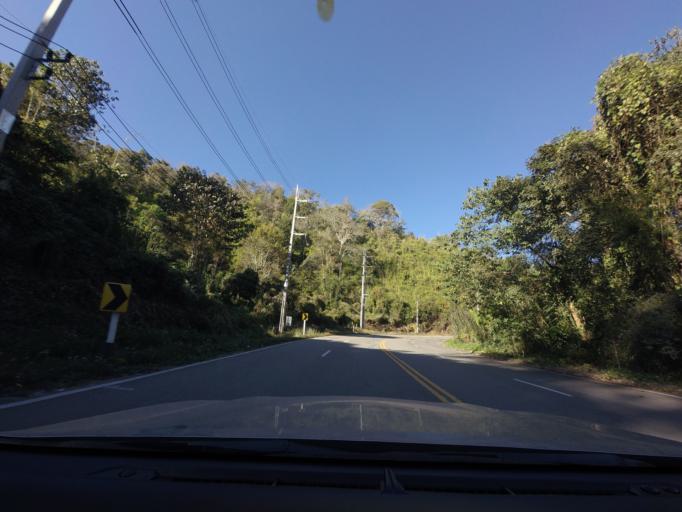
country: TH
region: Mae Hong Son
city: Mae Hi
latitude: 19.2160
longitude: 98.6693
